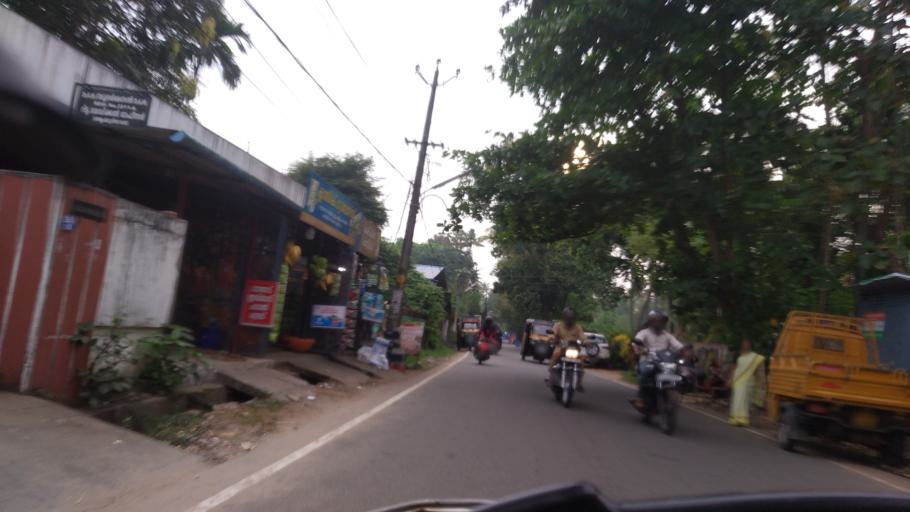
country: IN
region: Kerala
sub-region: Thrissur District
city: Kodungallur
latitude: 10.1398
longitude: 76.2292
